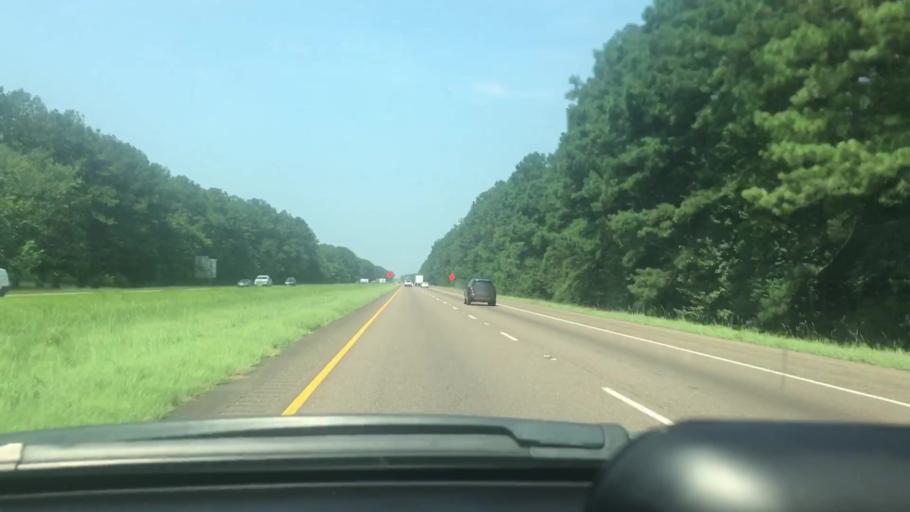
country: US
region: Louisiana
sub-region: Livingston Parish
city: Livingston
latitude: 30.4742
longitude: -90.7662
